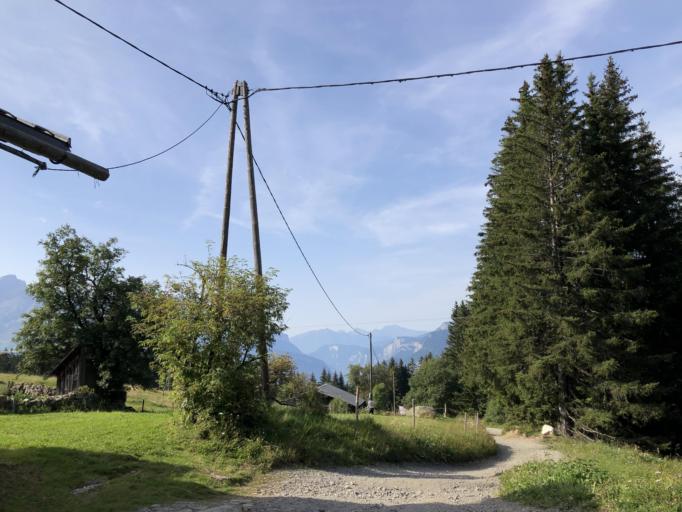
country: FR
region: Rhone-Alpes
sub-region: Departement de la Haute-Savoie
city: Combloux
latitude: 45.8758
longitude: 6.6611
